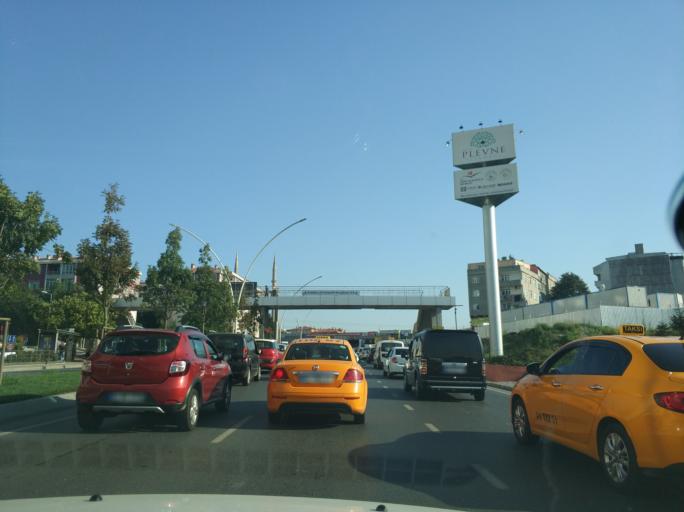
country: TR
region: Istanbul
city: Sultangazi
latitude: 41.0871
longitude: 28.9079
